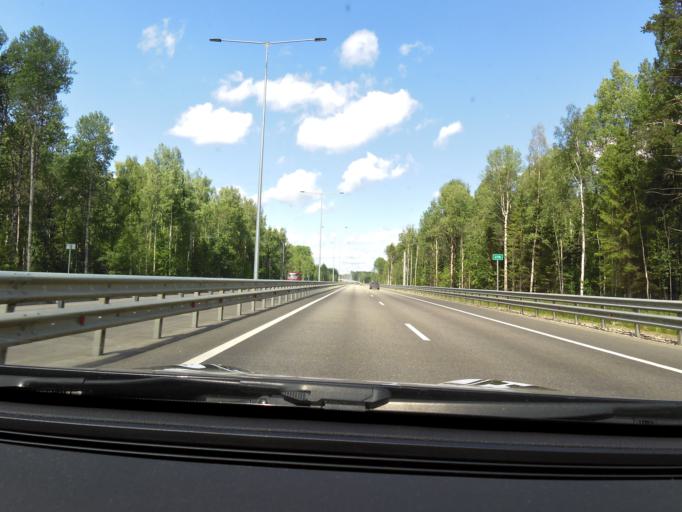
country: RU
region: Tverskaya
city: Vydropuzhsk
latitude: 57.3489
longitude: 34.7077
